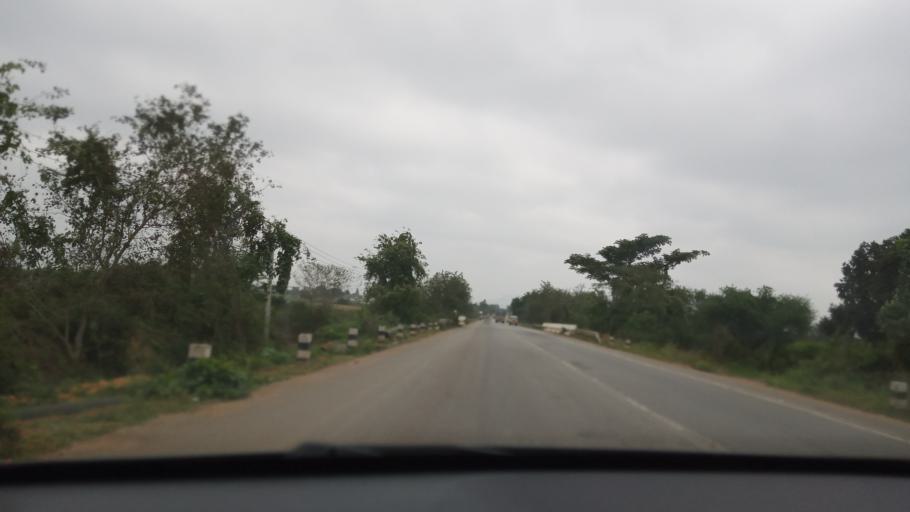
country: IN
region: Karnataka
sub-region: Chikkaballapur
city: Sidlaghatta
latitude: 13.2778
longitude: 77.9545
